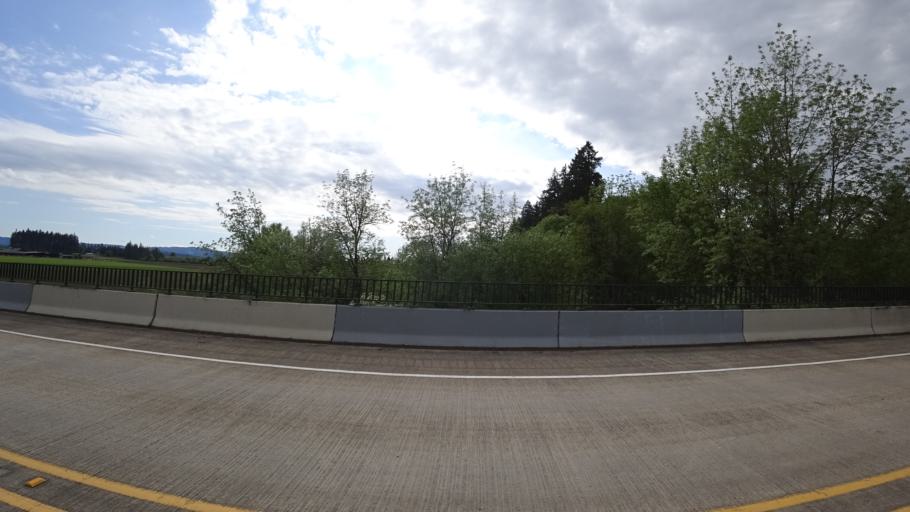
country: US
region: Oregon
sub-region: Washington County
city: Hillsboro
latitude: 45.4902
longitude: -122.9518
